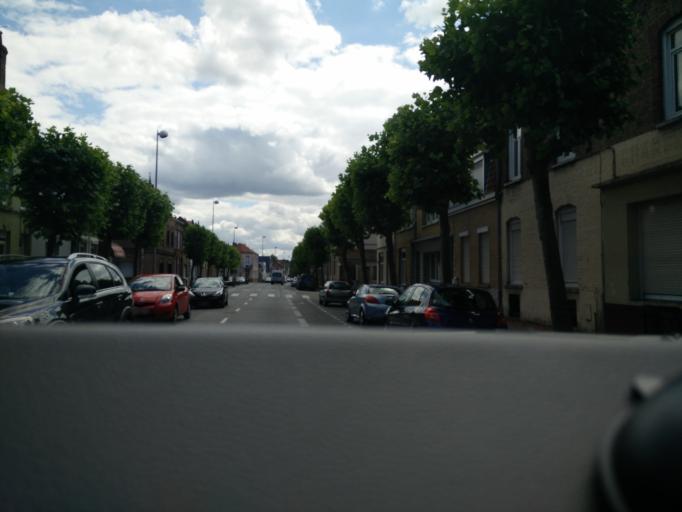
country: FR
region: Nord-Pas-de-Calais
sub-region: Departement du Nord
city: Coudekerque-Branche
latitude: 51.0444
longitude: 2.4038
